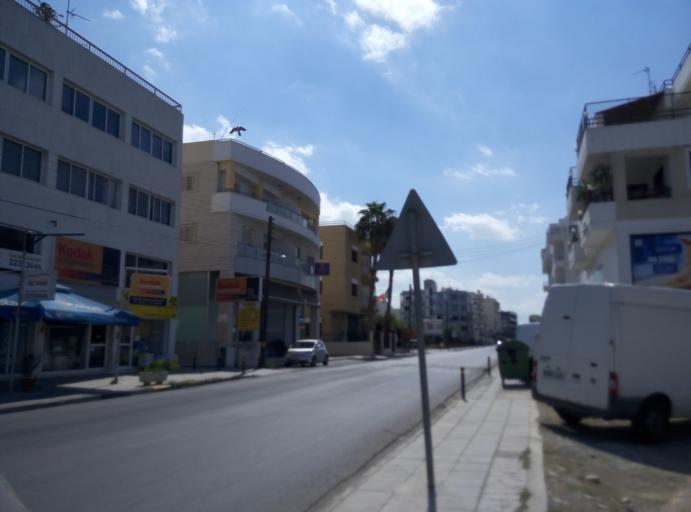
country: CY
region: Lefkosia
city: Nicosia
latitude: 35.1675
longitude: 33.3308
